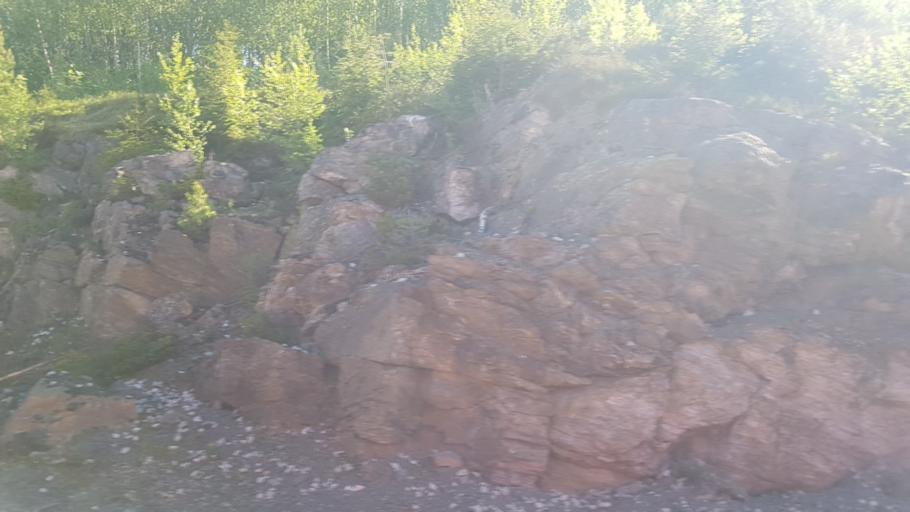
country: NO
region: Sor-Trondelag
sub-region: Rennebu
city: Berkak
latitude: 62.8286
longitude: 10.0119
